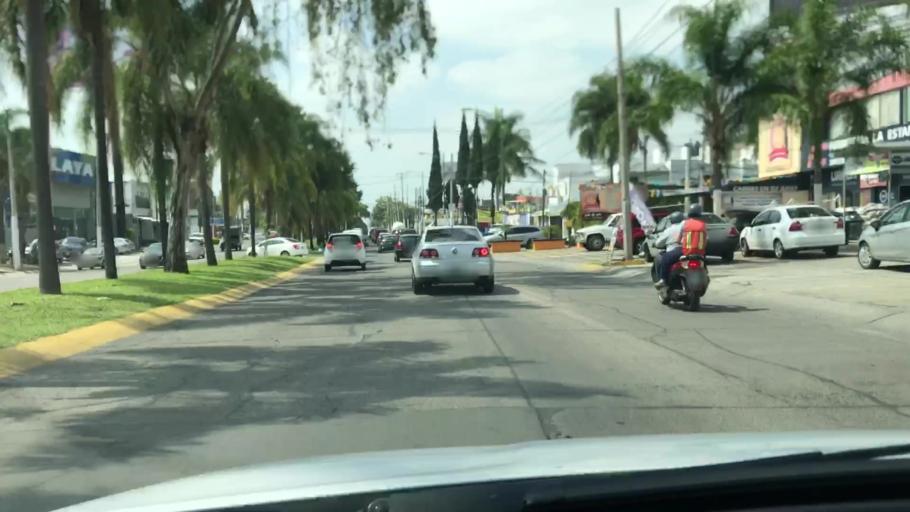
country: MX
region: Jalisco
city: Guadalajara
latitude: 20.6686
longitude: -103.4246
